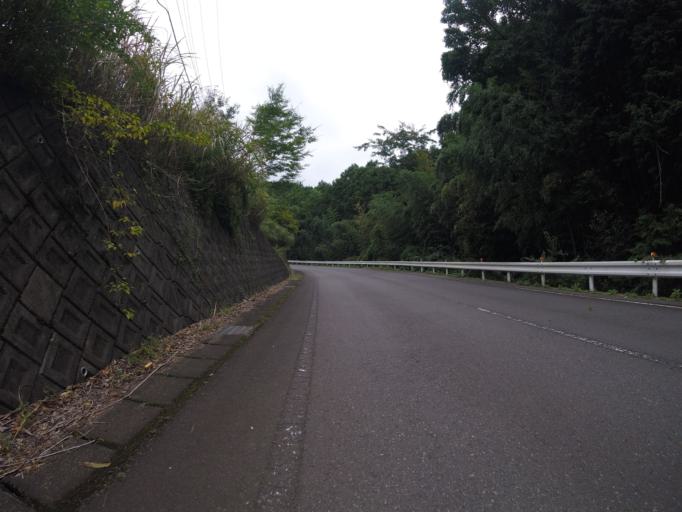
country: JP
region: Shizuoka
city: Mishima
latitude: 35.1345
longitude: 138.9709
